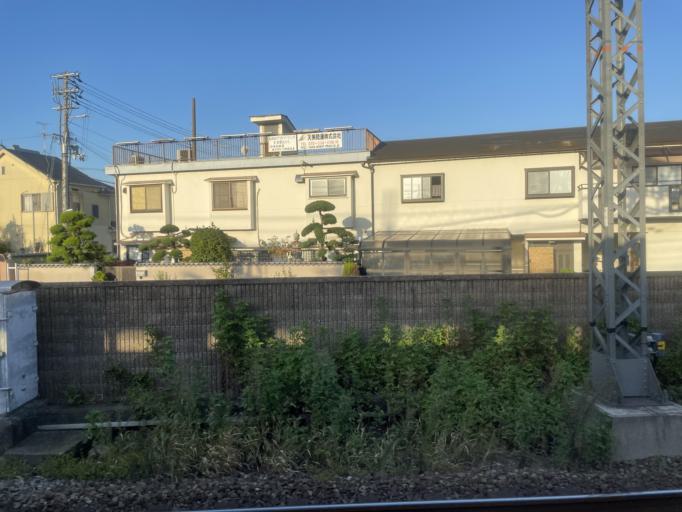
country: JP
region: Osaka
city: Matsubara
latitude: 34.5840
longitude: 135.5364
